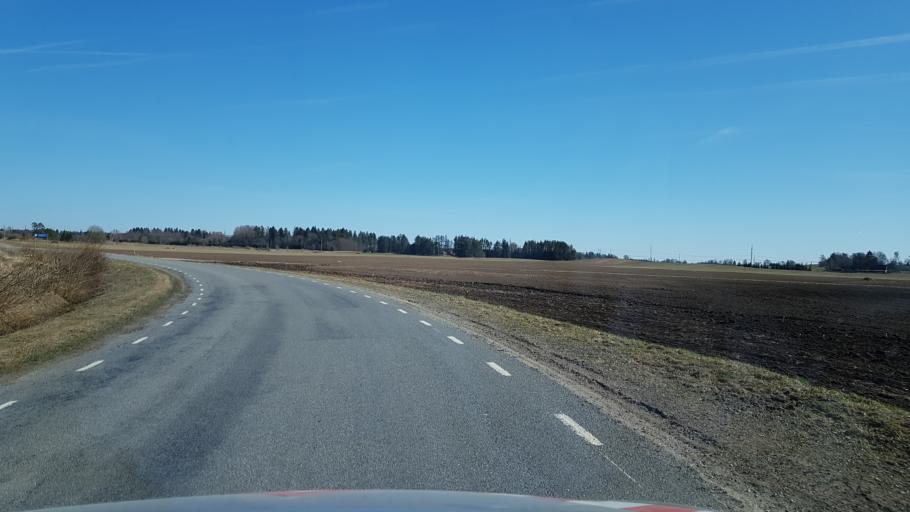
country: EE
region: Laeaene-Virumaa
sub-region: Someru vald
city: Someru
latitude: 59.3346
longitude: 26.5243
